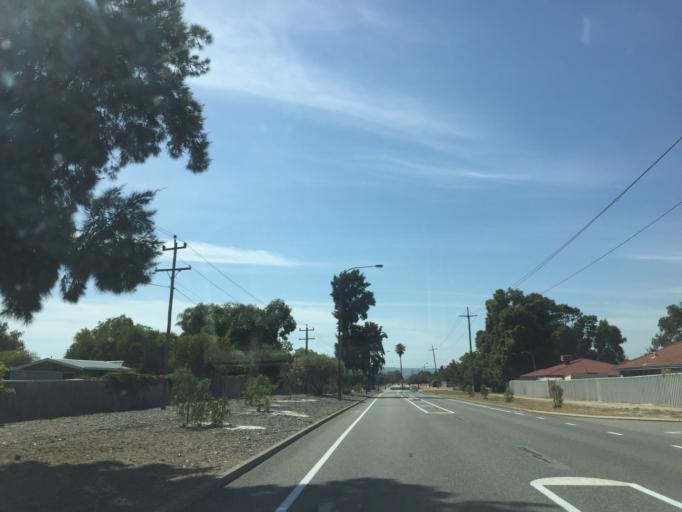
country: AU
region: Western Australia
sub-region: Gosnells
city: Thornlie
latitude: -32.0770
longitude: 115.9635
